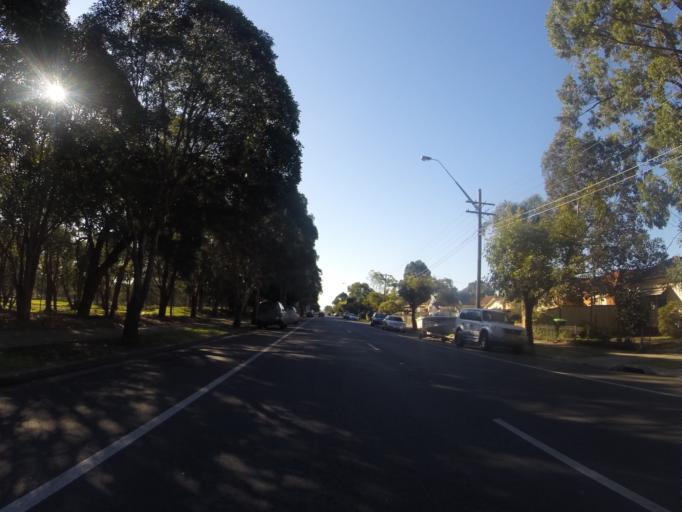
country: AU
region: New South Wales
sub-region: Bankstown
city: Regents Park
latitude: -33.8686
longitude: 151.0176
